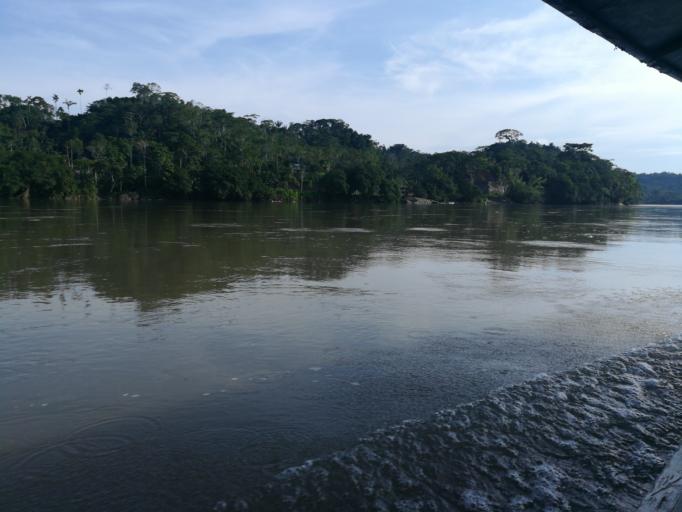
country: EC
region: Orellana
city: Boca Suno
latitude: -0.8584
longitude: -77.2459
